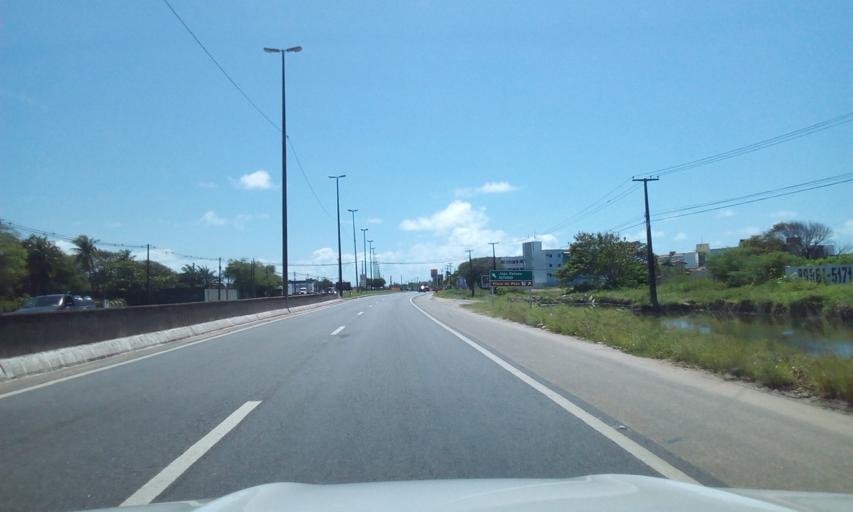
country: BR
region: Paraiba
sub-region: Cabedelo
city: Cabedelo
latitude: -7.0234
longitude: -34.8372
